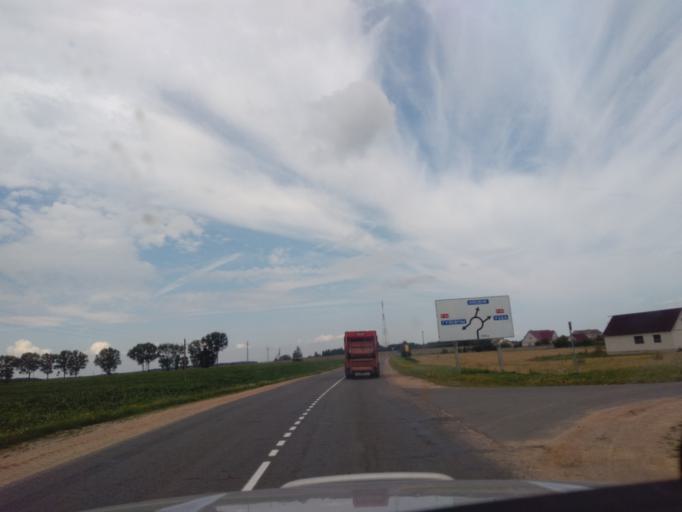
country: BY
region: Minsk
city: Kapyl'
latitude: 53.1356
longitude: 27.0924
